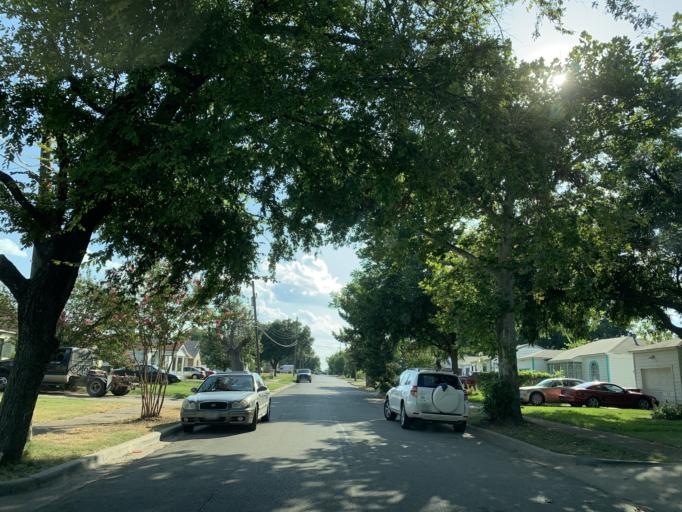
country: US
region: Texas
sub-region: Dallas County
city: Hutchins
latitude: 32.6983
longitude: -96.7770
